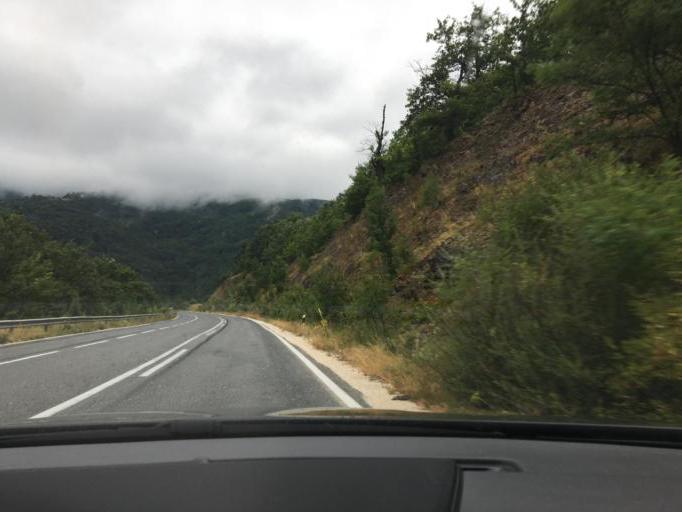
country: MK
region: Kriva Palanka
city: Kriva Palanka
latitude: 42.2206
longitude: 22.4408
